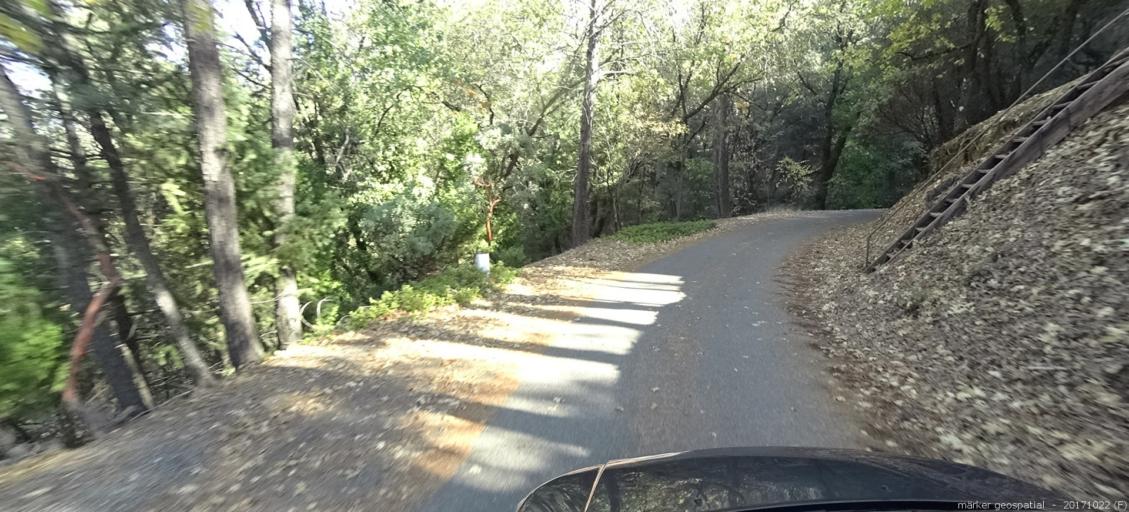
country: US
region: California
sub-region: Shasta County
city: Shasta Lake
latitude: 40.8397
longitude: -122.3658
